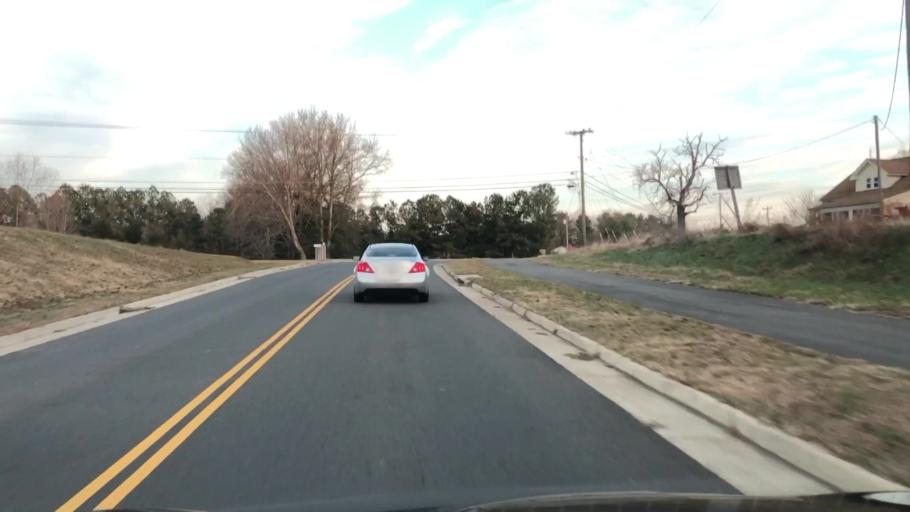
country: US
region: Virginia
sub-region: Stafford County
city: Falmouth
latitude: 38.3702
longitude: -77.4903
